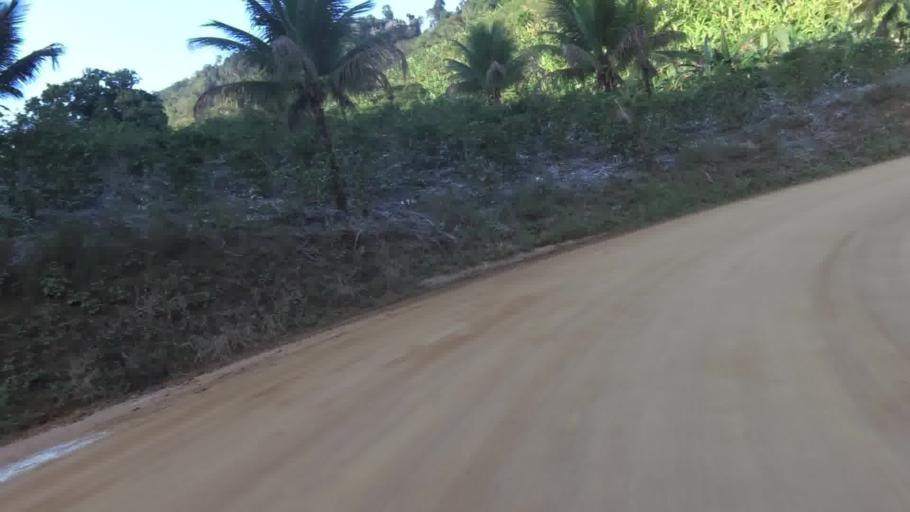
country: BR
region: Espirito Santo
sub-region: Alfredo Chaves
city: Alfredo Chaves
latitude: -20.5924
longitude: -40.6971
